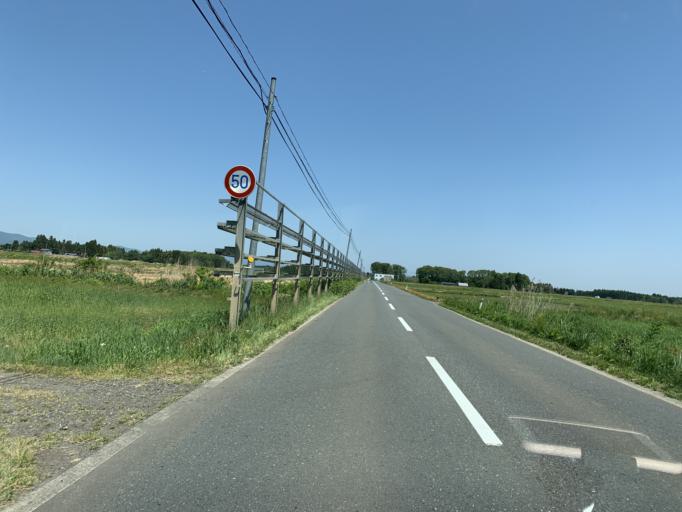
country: JP
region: Iwate
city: Kitakami
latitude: 39.2557
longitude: 141.0648
